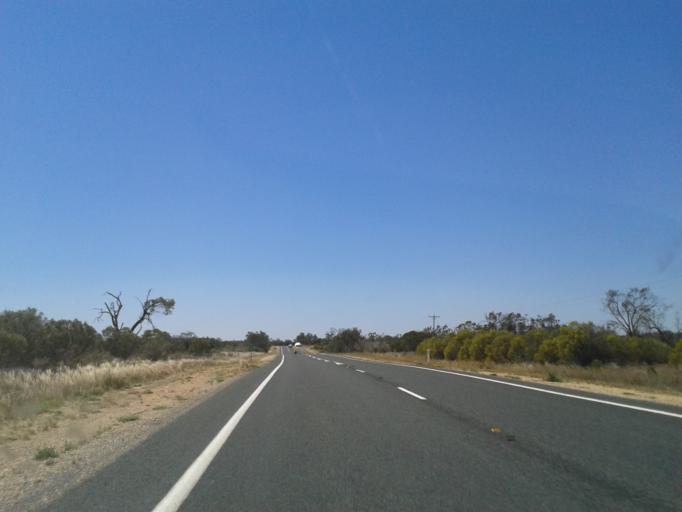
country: AU
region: New South Wales
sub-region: Wentworth
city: Dareton
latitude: -34.0981
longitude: 142.0821
